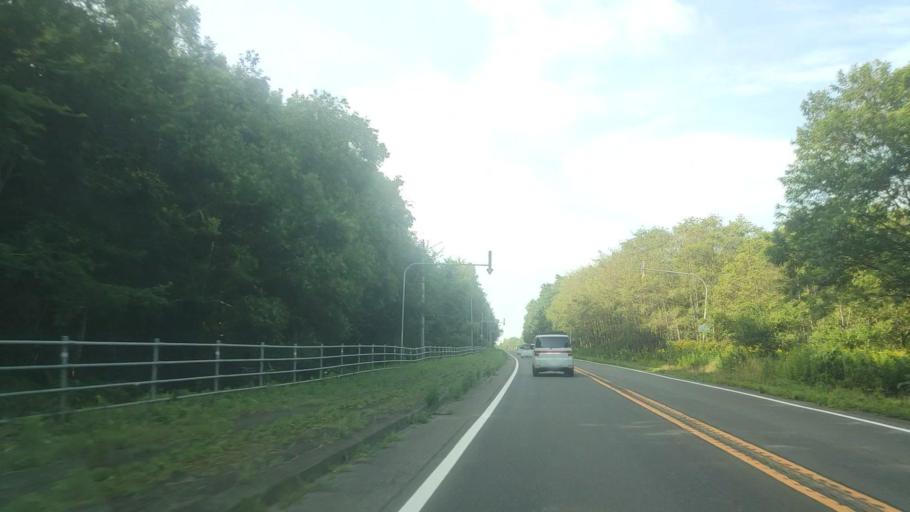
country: JP
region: Hokkaido
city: Chitose
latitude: 42.8627
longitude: 141.8225
